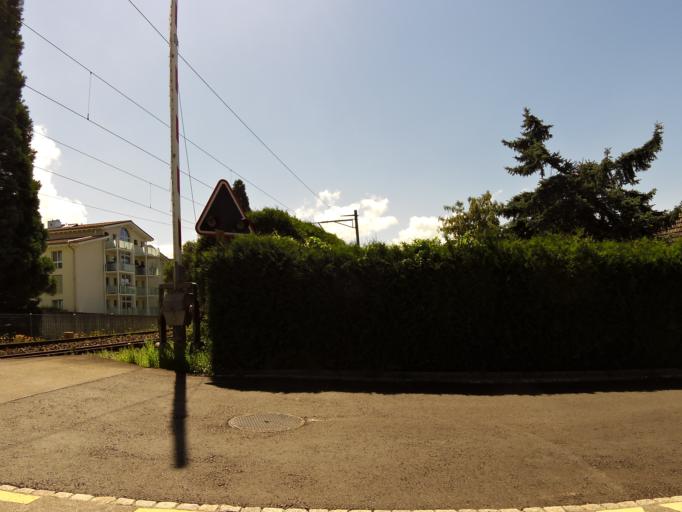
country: CH
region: Appenzell Ausserrhoden
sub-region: Bezirk Vorderland
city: Heiden
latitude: 47.4822
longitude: 9.5419
